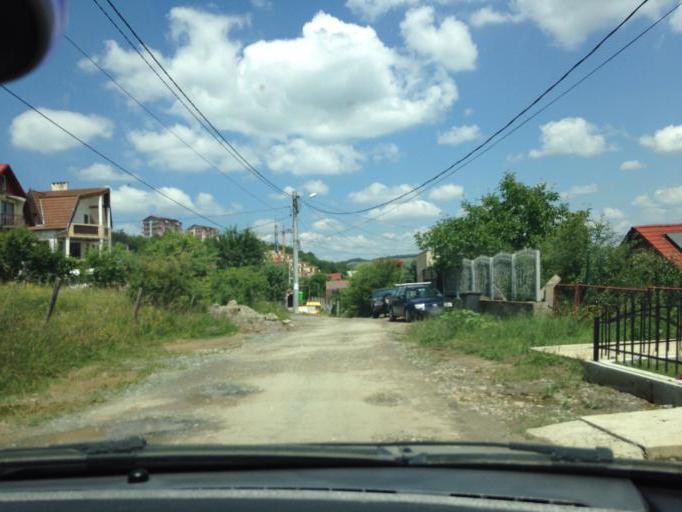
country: RO
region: Cluj
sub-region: Comuna Floresti
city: Floresti
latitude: 46.7421
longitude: 23.5323
